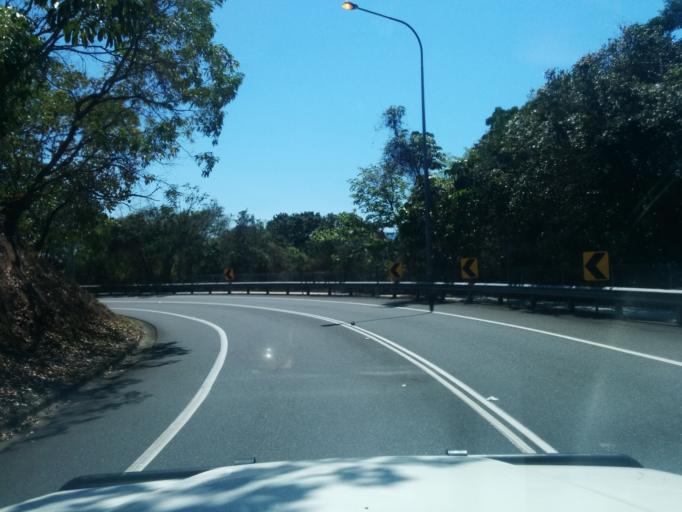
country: AU
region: Queensland
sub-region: Cairns
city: Woree
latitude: -16.9549
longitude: 145.7368
